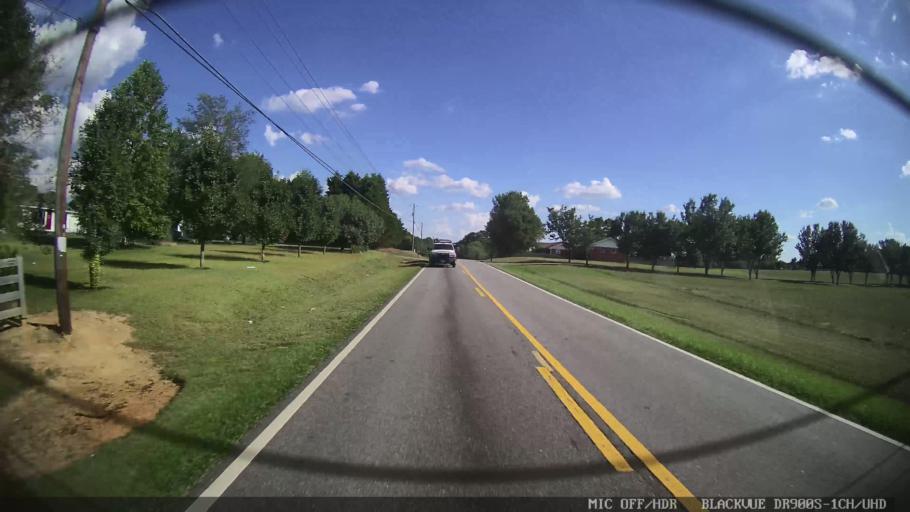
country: US
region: Georgia
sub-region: Bartow County
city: Euharlee
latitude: 34.1404
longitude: -84.9781
